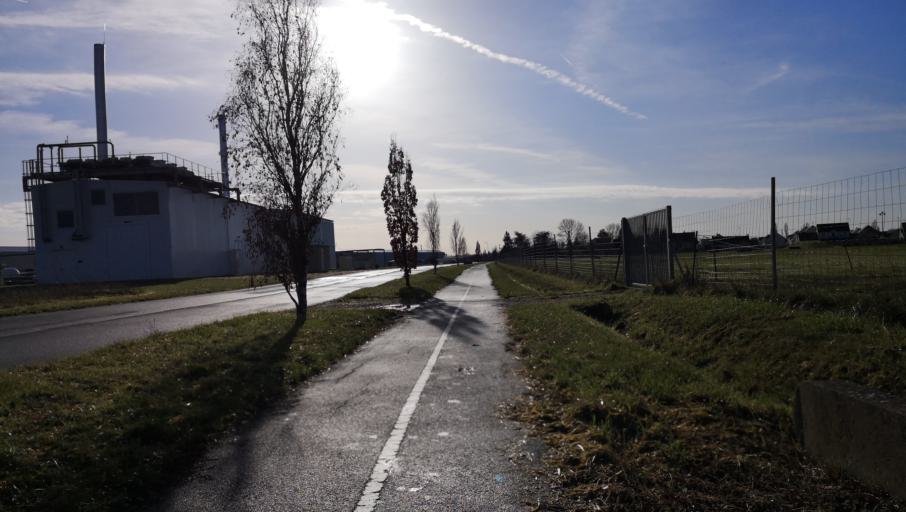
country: FR
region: Centre
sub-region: Departement du Loiret
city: Saint-Denis-en-Val
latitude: 47.8754
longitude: 1.9795
